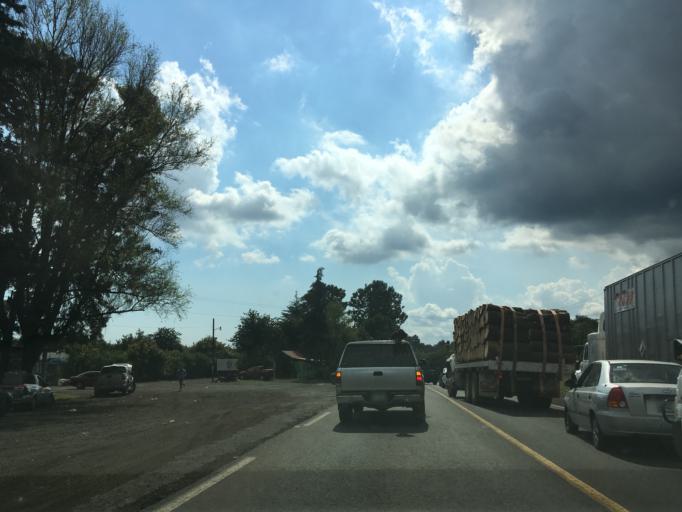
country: MX
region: Michoacan
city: Tingambato
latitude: 19.5008
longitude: -101.8686
